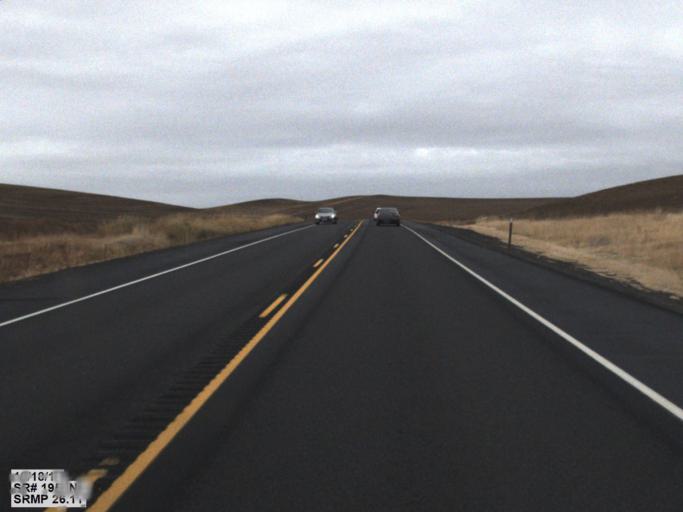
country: US
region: Washington
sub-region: Whitman County
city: Pullman
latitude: 46.7557
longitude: -117.2395
